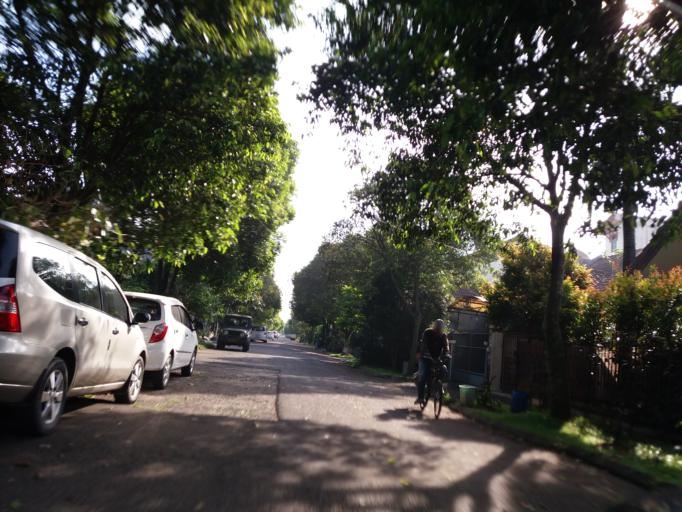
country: ID
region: West Java
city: Pameungpeuk
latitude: -6.9639
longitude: 107.6325
